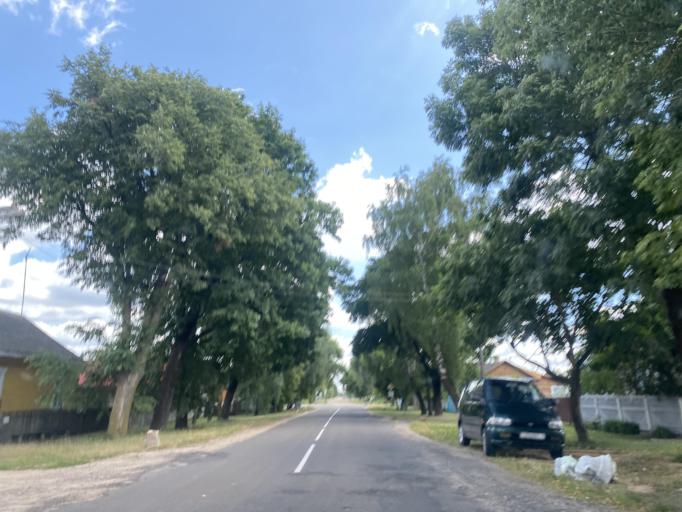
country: BY
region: Brest
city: Ivanava
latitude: 52.1677
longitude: 25.5572
